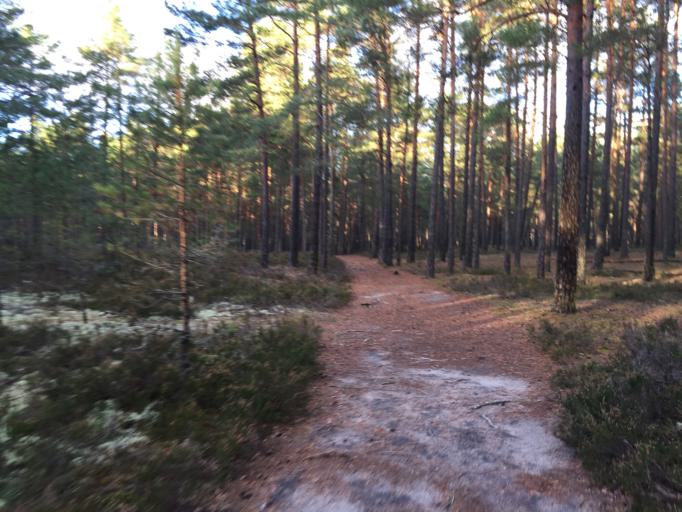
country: LV
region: Carnikava
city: Carnikava
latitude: 57.1716
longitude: 24.3357
